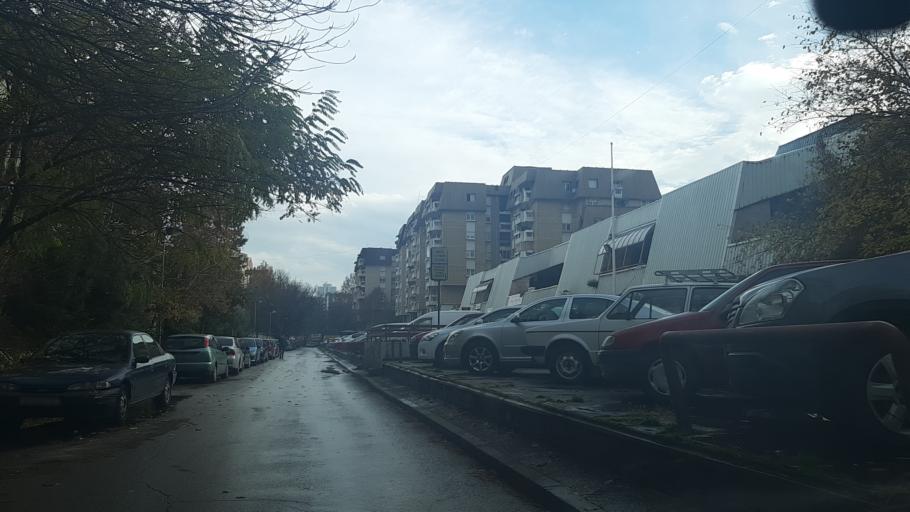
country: MK
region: Karpos
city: Skopje
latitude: 41.9895
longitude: 21.4501
